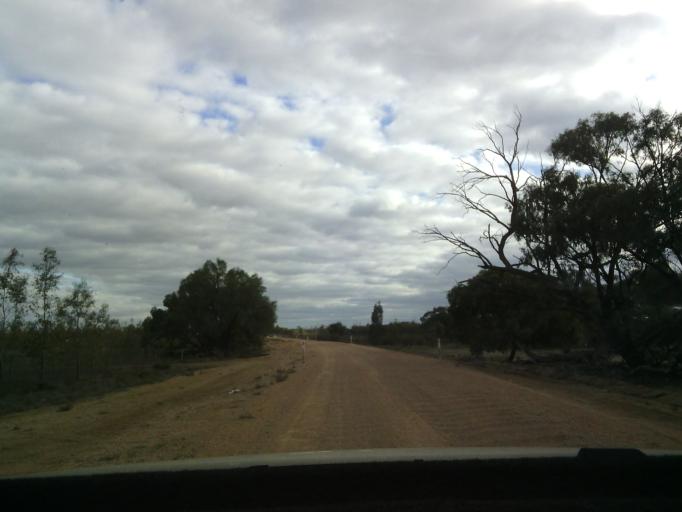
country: AU
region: South Australia
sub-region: Renmark Paringa
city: Renmark
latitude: -34.1631
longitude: 141.1988
